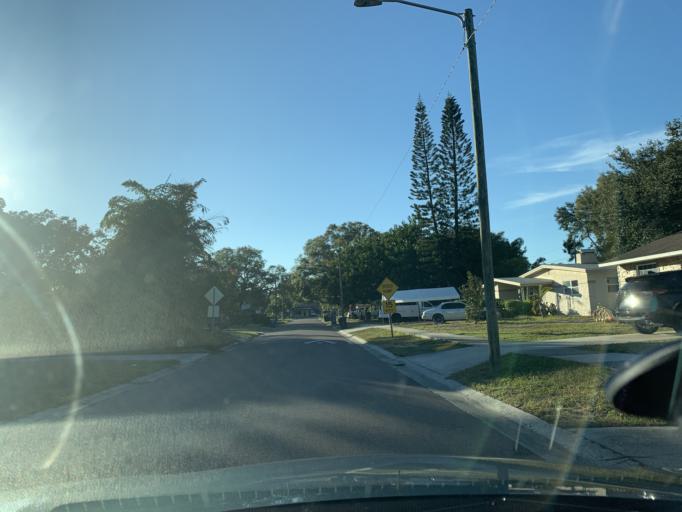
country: US
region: Florida
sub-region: Pinellas County
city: Gulfport
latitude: 27.7469
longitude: -82.6979
